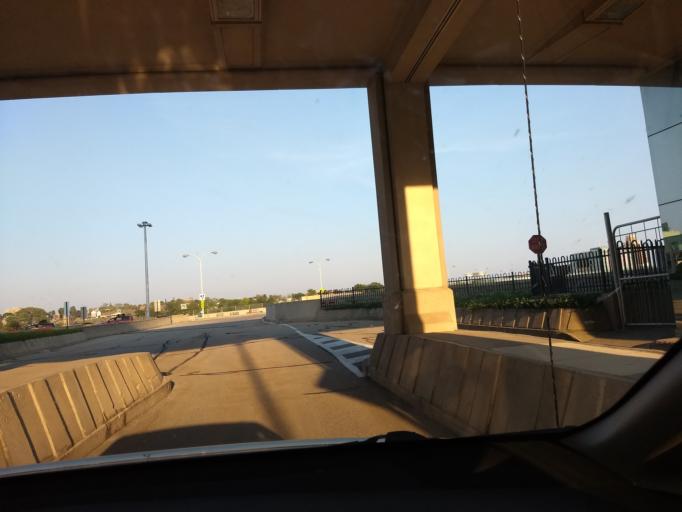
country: CA
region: Ontario
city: Niagara Falls
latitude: 43.0915
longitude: -79.0703
